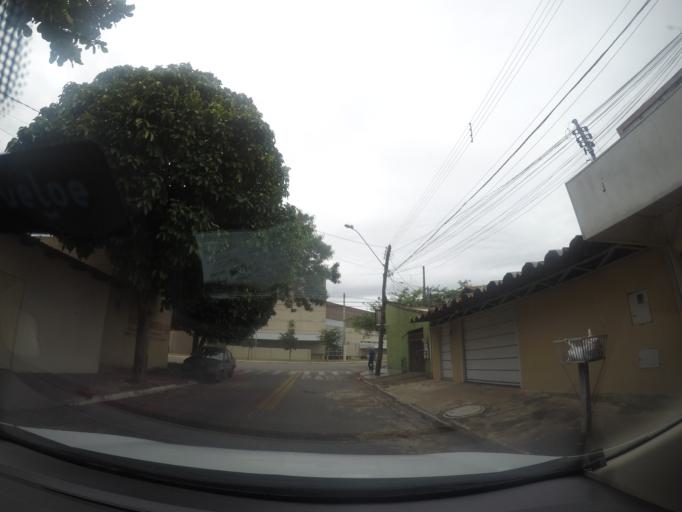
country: BR
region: Goias
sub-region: Goiania
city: Goiania
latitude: -16.6645
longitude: -49.3078
